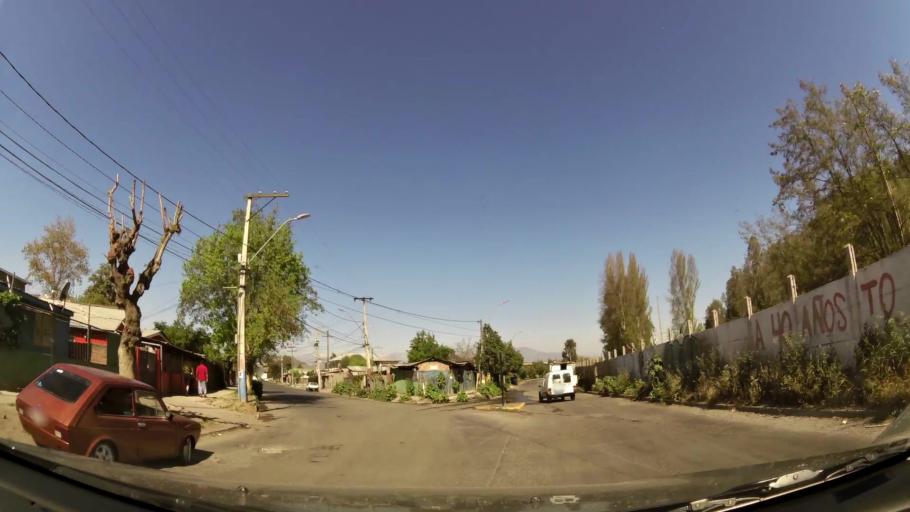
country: CL
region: Santiago Metropolitan
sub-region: Provincia de Maipo
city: San Bernardo
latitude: -33.6067
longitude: -70.7138
